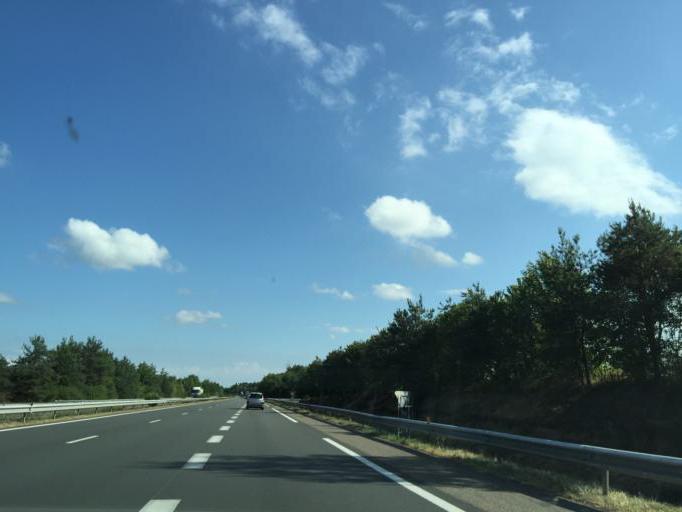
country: FR
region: Rhone-Alpes
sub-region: Departement de la Loire
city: Balbigny
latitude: 45.8144
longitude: 4.1166
